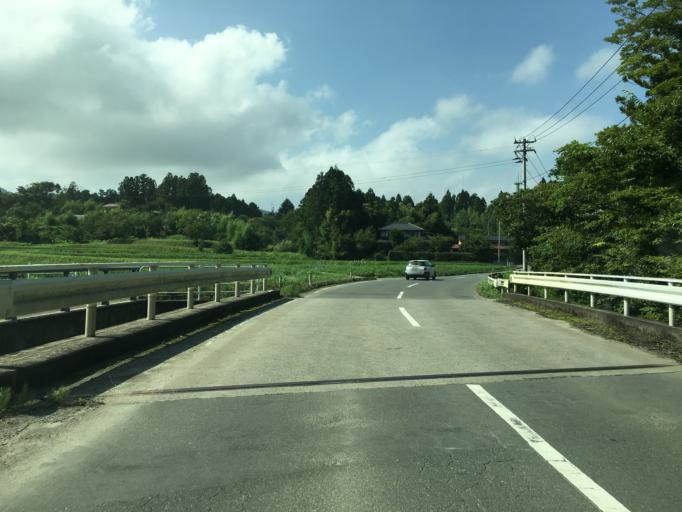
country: JP
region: Miyagi
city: Marumori
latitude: 37.8619
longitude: 140.8926
